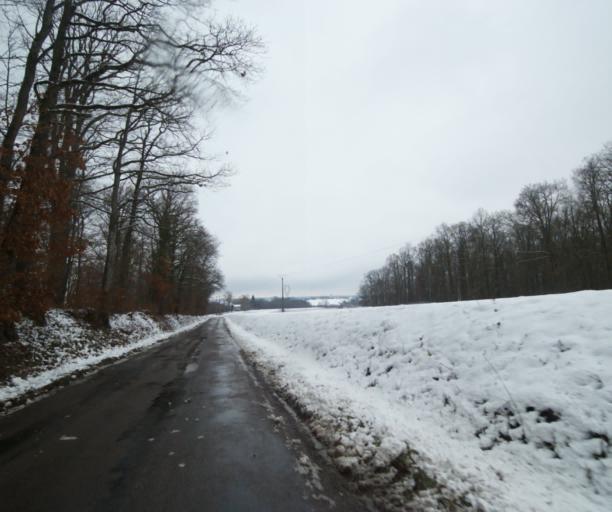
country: FR
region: Champagne-Ardenne
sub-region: Departement de la Haute-Marne
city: Laneuville-a-Remy
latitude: 48.5170
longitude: 4.8389
